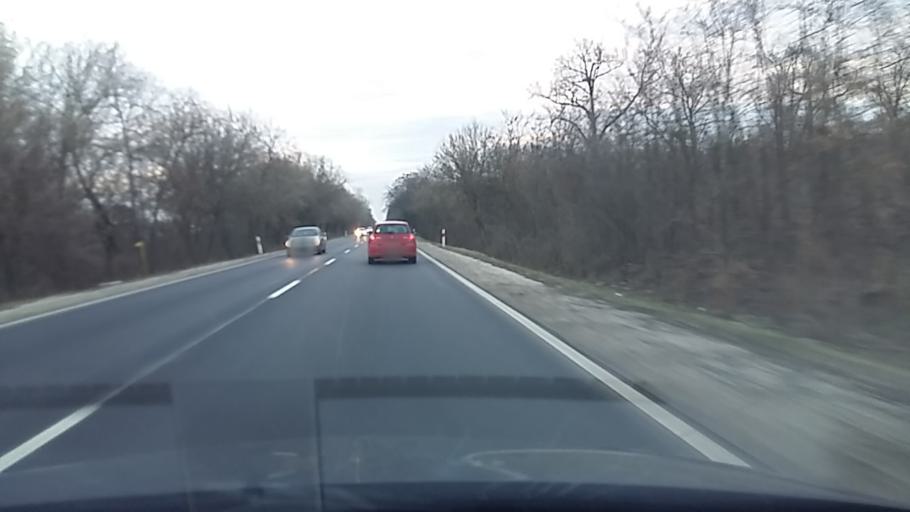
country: HU
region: Hajdu-Bihar
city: Debrecen
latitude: 47.5670
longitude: 21.6522
